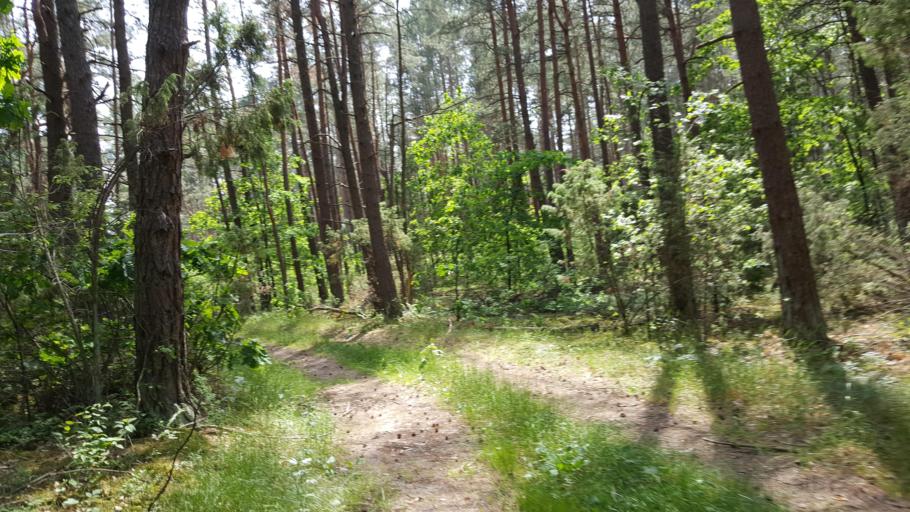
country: BY
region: Brest
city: Kamyanyuki
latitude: 52.5098
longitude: 23.8274
